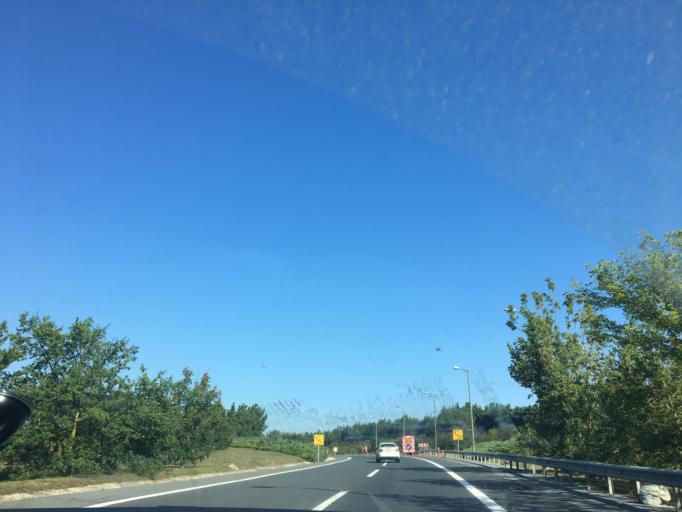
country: TR
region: Istanbul
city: Silivri
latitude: 41.1196
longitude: 28.1922
